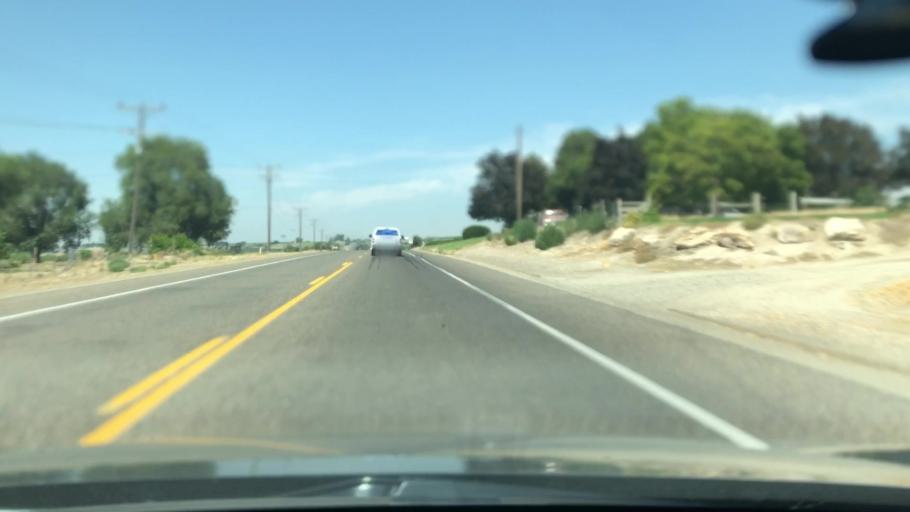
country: US
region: Idaho
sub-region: Owyhee County
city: Homedale
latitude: 43.6385
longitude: -116.9117
